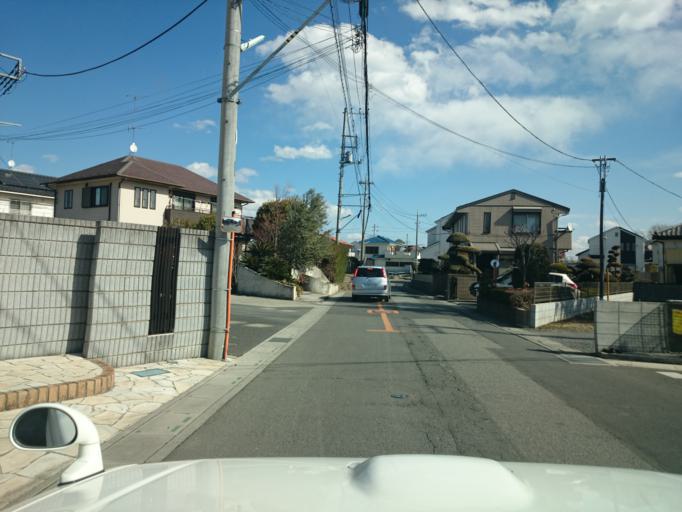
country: JP
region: Saitama
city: Kukichuo
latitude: 36.0590
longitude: 139.7007
